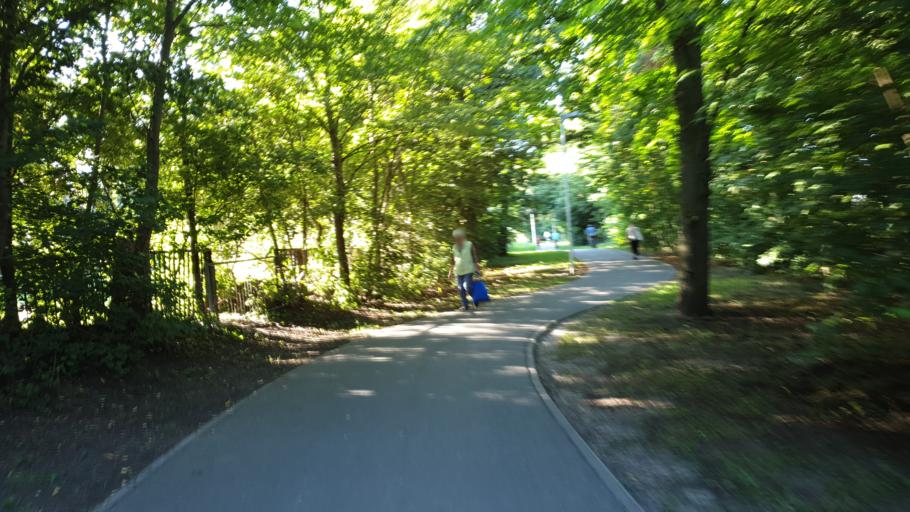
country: DE
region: Mecklenburg-Vorpommern
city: Stralsund
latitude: 54.3319
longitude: 13.0810
